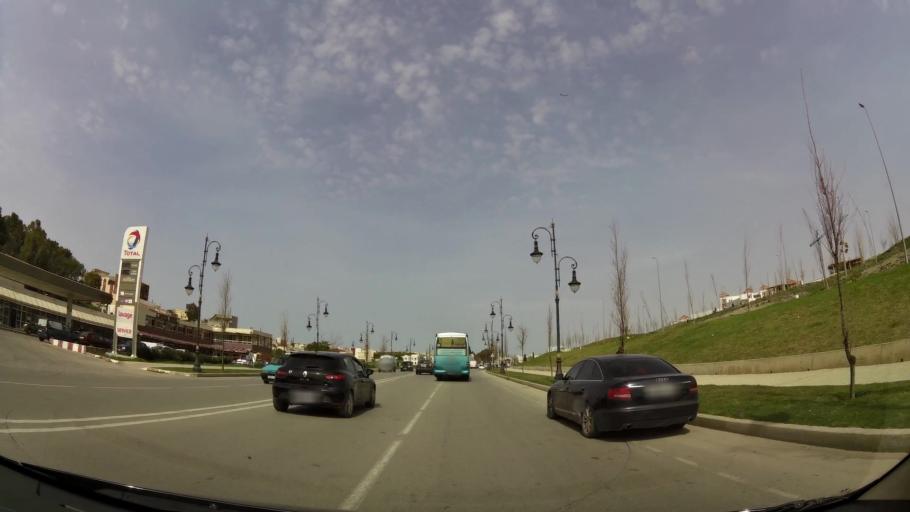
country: MA
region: Tanger-Tetouan
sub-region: Tanger-Assilah
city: Boukhalef
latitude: 35.7418
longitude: -5.8671
